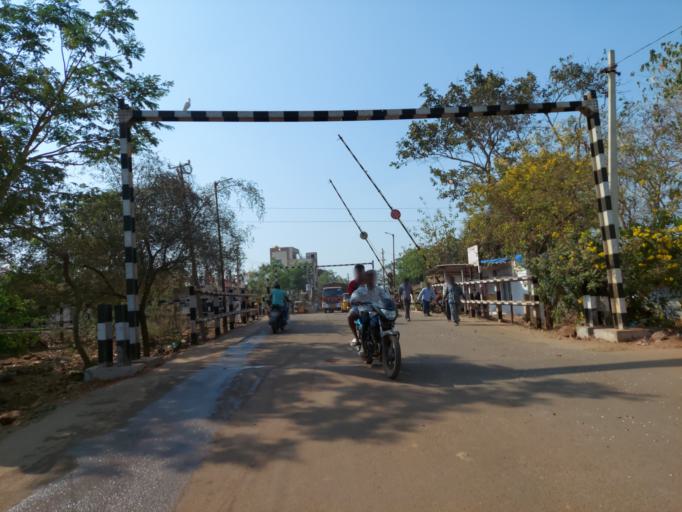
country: IN
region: Telangana
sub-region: Rangareddi
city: Vikarabad
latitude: 17.3383
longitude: 77.8990
